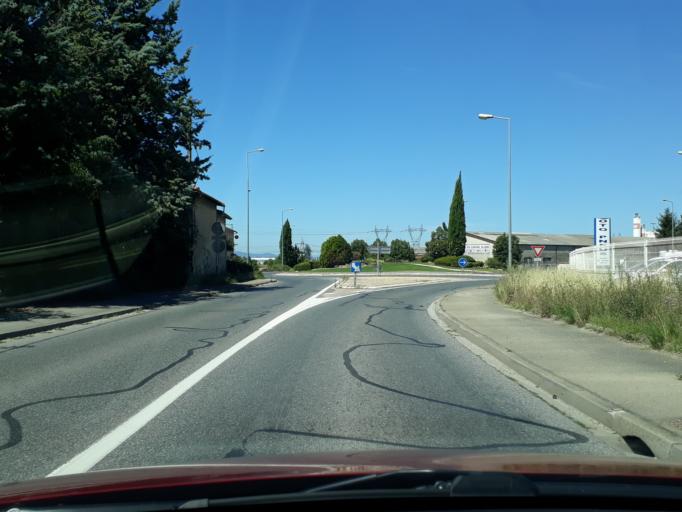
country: FR
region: Rhone-Alpes
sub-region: Departement du Rhone
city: Toussieu
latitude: 45.6696
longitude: 4.9827
